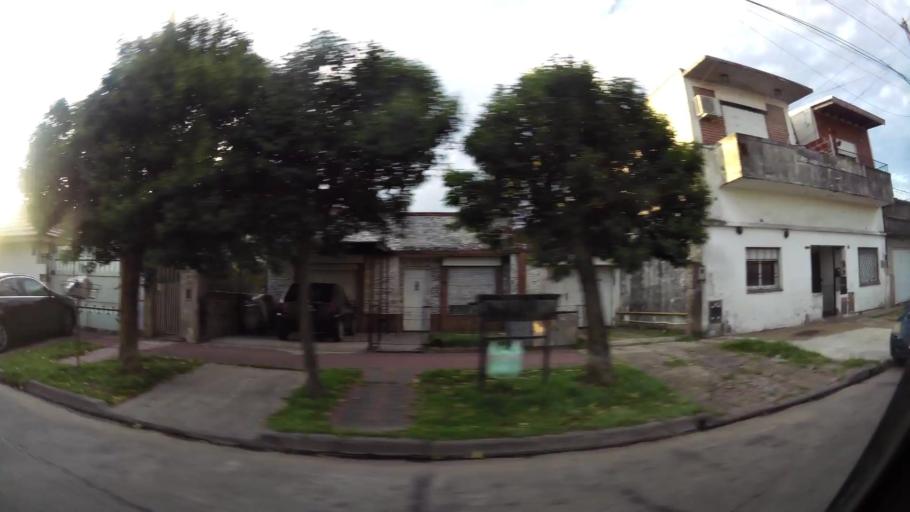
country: AR
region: Buenos Aires
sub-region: Partido de Lanus
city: Lanus
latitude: -34.7127
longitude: -58.3378
